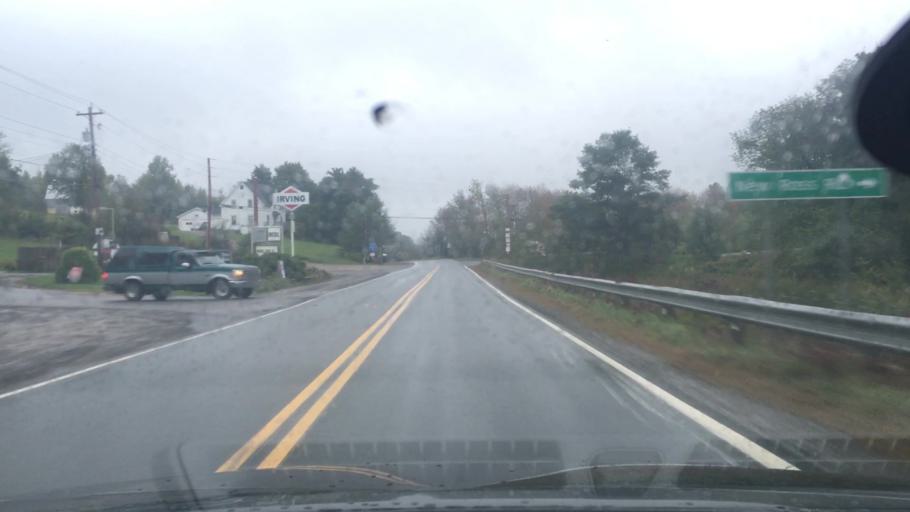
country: CA
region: Nova Scotia
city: Windsor
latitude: 44.8416
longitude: -64.2305
